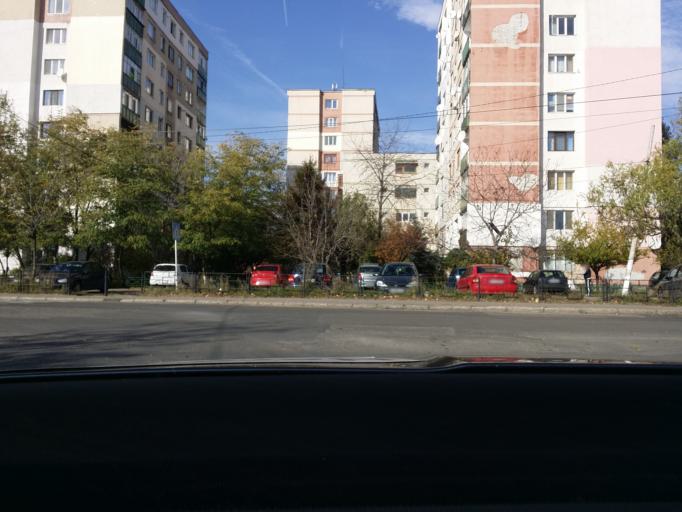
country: RO
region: Prahova
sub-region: Municipiul Campina
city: Campina
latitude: 45.1197
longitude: 25.7419
